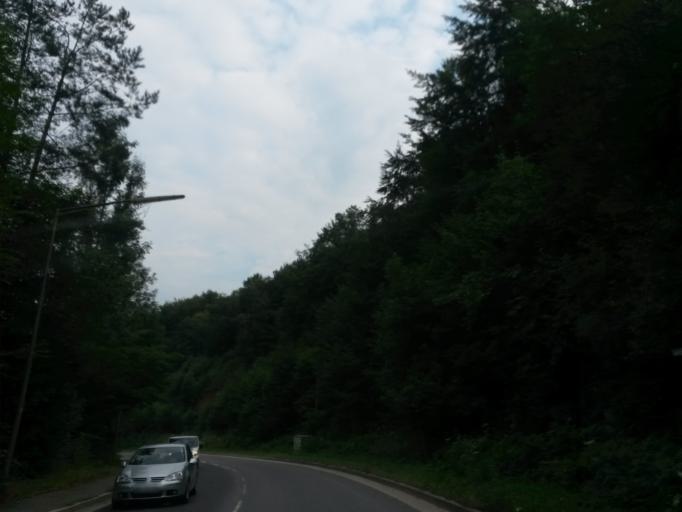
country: DE
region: North Rhine-Westphalia
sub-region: Regierungsbezirk Koln
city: Gummersbach
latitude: 51.0421
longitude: 7.5866
